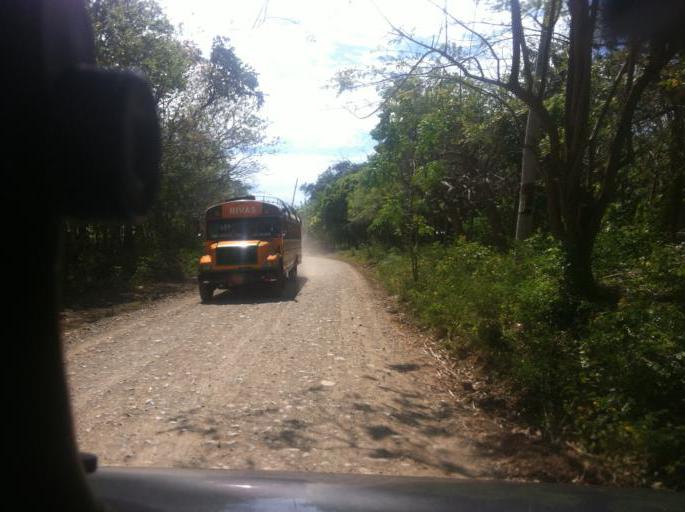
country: NI
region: Rivas
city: Tola
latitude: 11.5315
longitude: -86.0580
